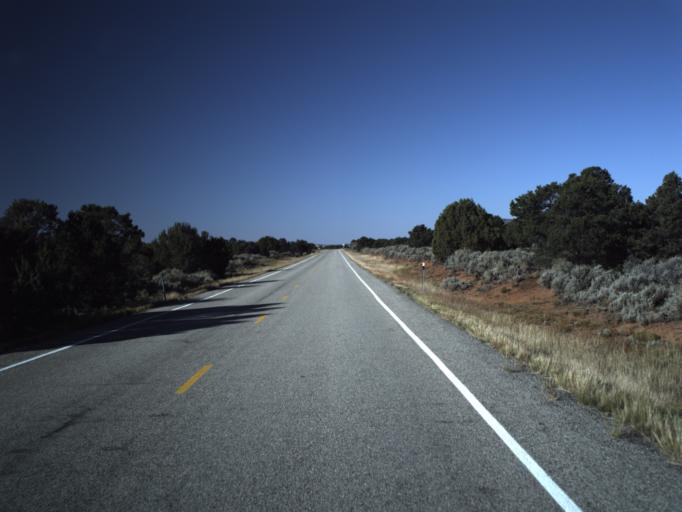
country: US
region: Utah
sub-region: San Juan County
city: Blanding
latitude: 37.5842
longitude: -109.9067
